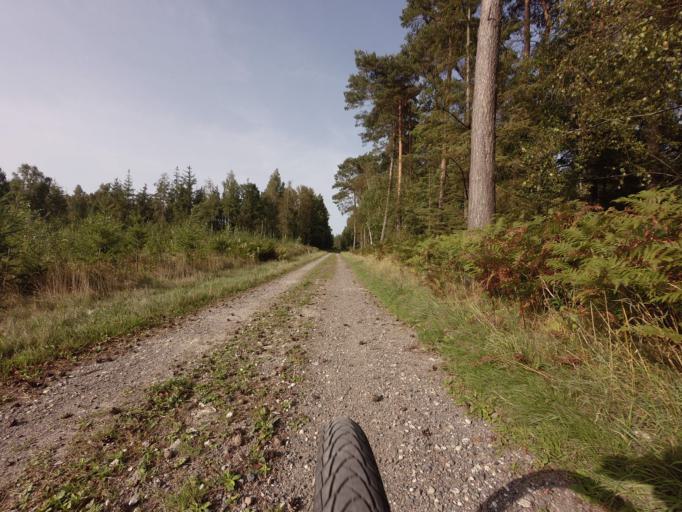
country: DK
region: Zealand
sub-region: Vordingborg Kommune
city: Praesto
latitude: 55.1492
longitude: 12.0993
